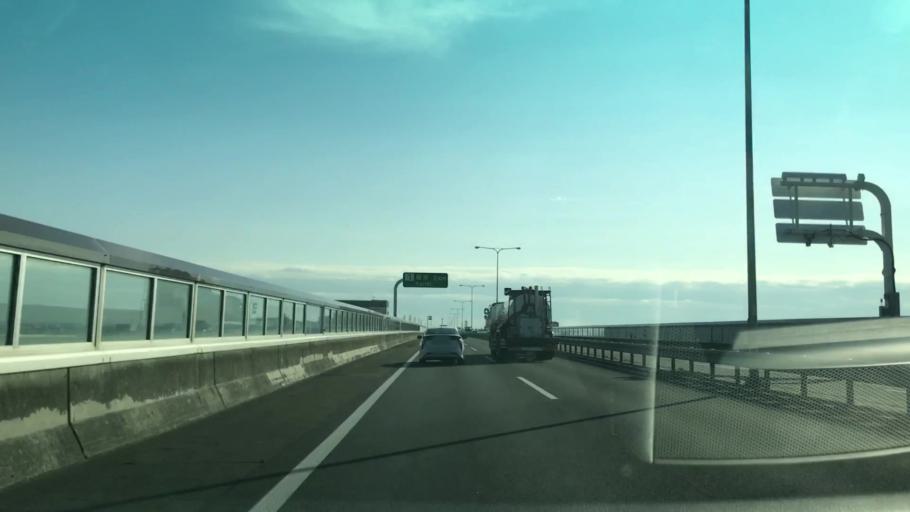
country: JP
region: Hokkaido
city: Sapporo
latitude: 43.1001
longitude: 141.3872
